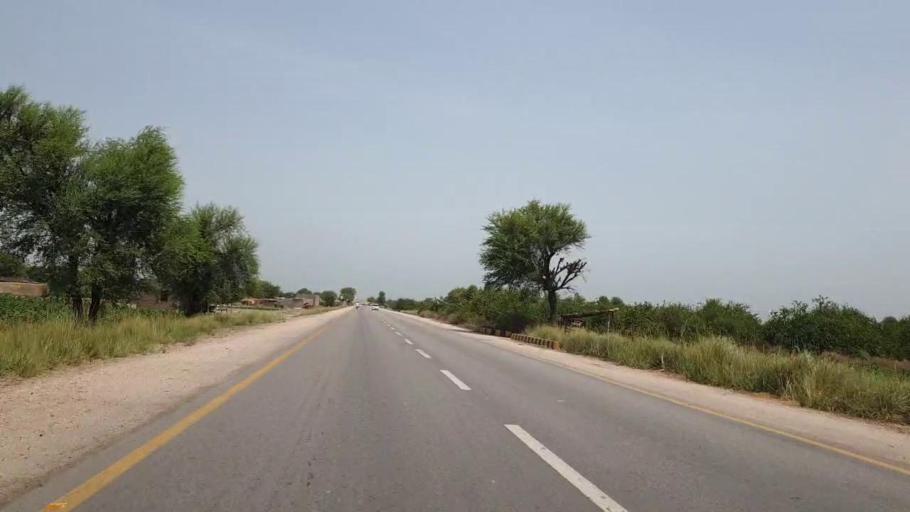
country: PK
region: Sindh
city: Shahpur Chakar
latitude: 26.1587
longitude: 68.6320
